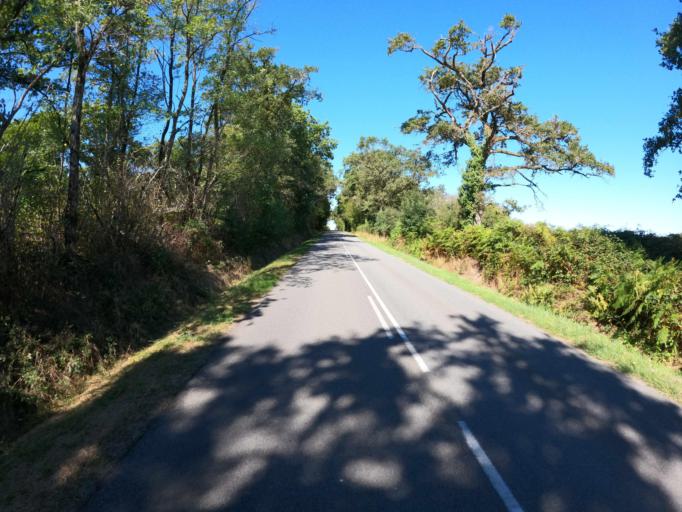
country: FR
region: Limousin
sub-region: Departement de la Haute-Vienne
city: Le Dorat
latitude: 46.2643
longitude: 1.0319
